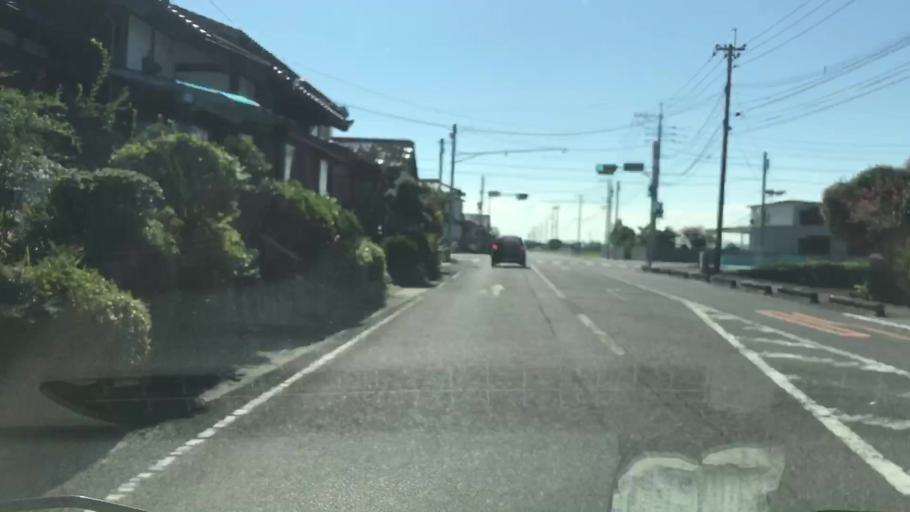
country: JP
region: Saga Prefecture
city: Okawa
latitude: 33.2194
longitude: 130.3351
